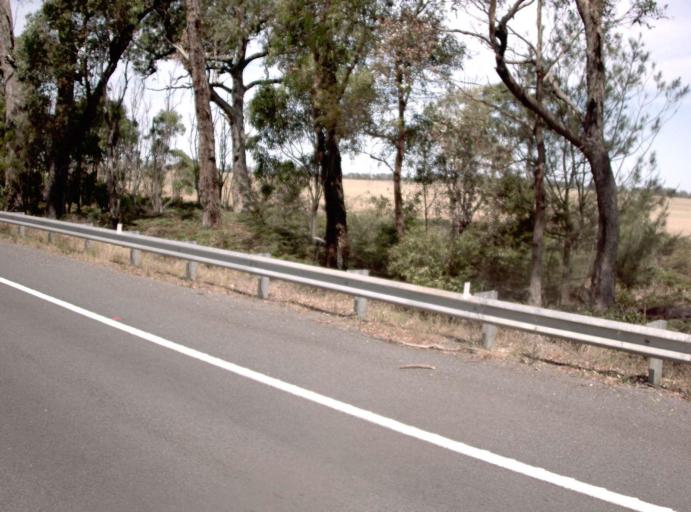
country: AU
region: Victoria
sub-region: Wellington
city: Sale
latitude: -37.9416
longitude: 147.1439
